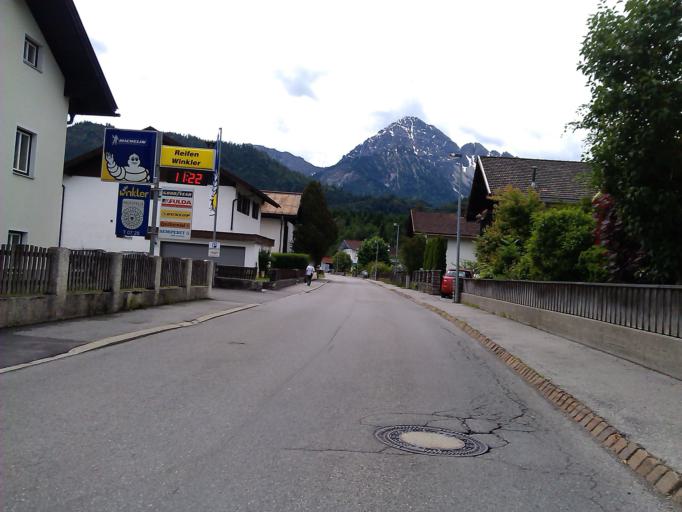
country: AT
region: Tyrol
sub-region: Politischer Bezirk Reutte
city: Reutte
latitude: 47.4817
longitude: 10.7205
